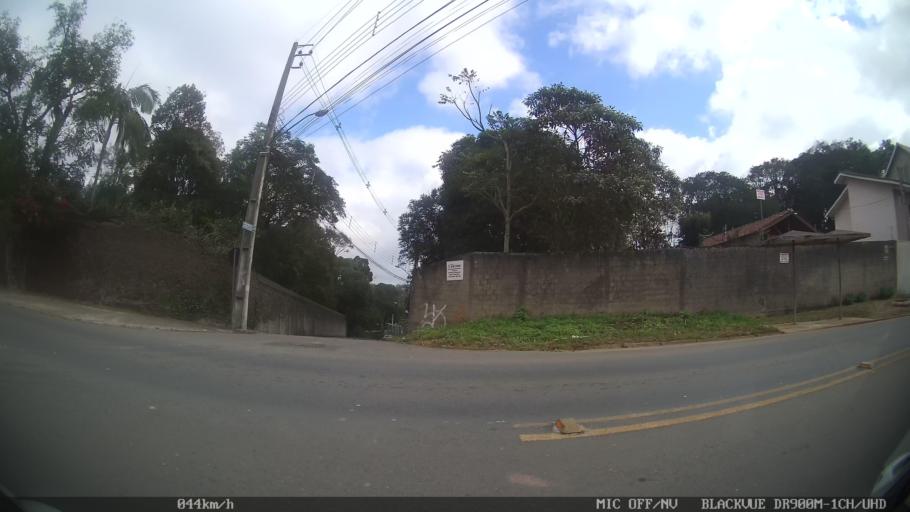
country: BR
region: Parana
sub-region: Curitiba
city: Curitiba
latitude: -25.3646
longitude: -49.2503
